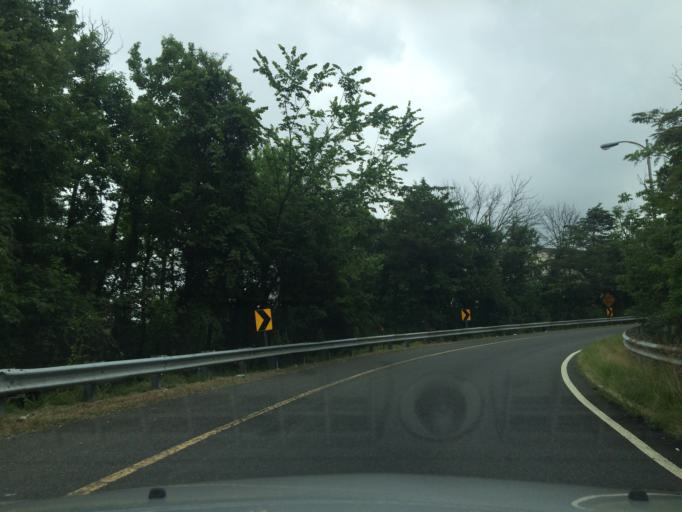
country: US
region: Maryland
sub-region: Prince George's County
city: Morningside
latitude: 38.8275
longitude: -76.8803
